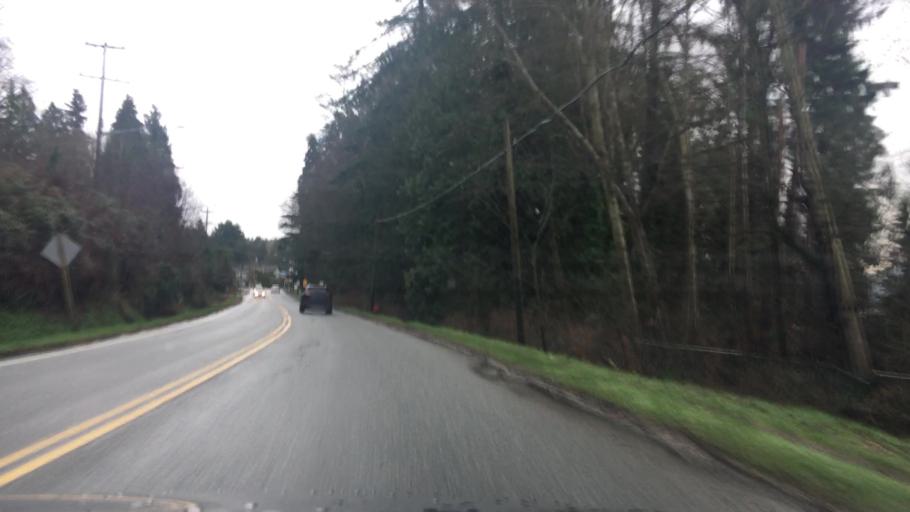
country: CA
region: British Columbia
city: Burnaby
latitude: 49.3083
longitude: -123.0003
